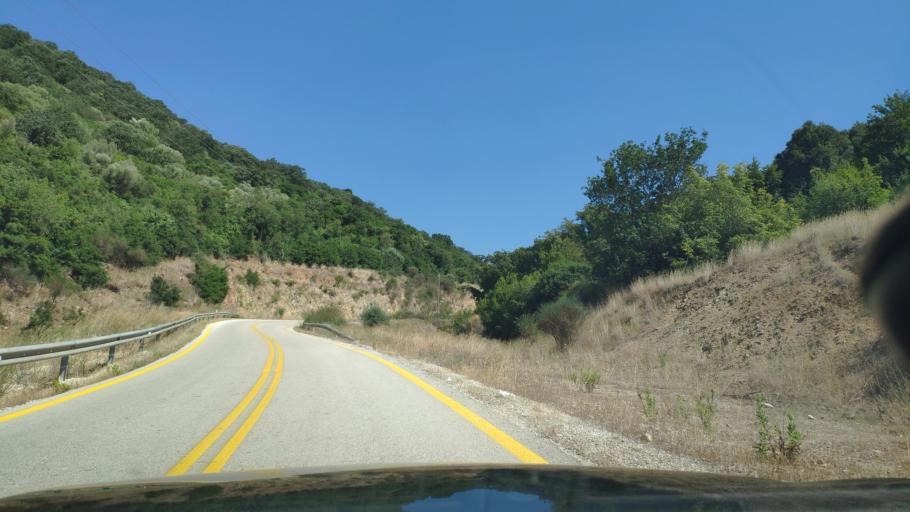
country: GR
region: West Greece
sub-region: Nomos Aitolias kai Akarnanias
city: Amfilochia
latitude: 38.8596
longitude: 21.0838
